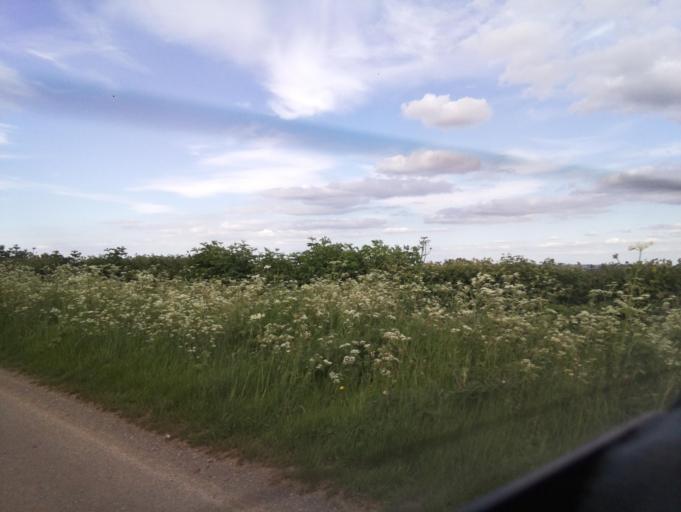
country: GB
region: England
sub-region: Gloucestershire
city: Moreton in Marsh
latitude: 52.0080
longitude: -1.7244
